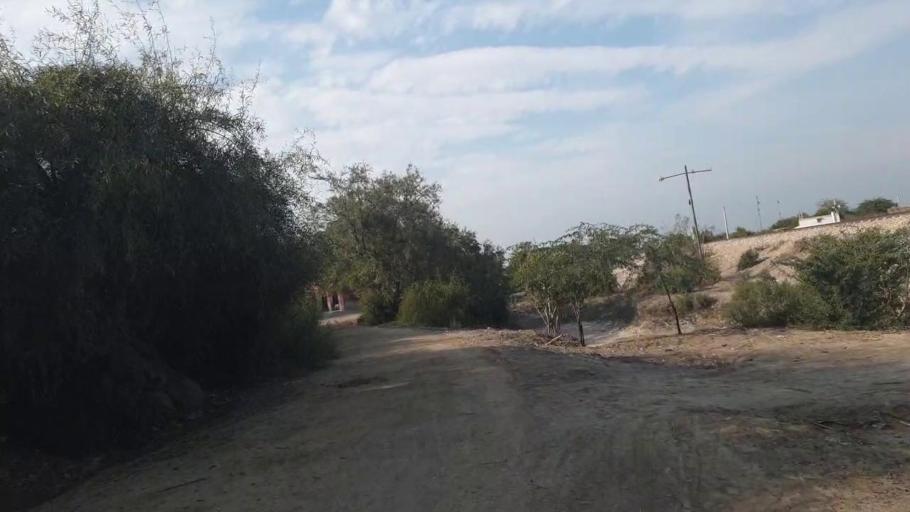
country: PK
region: Sindh
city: Shahdadpur
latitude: 26.0410
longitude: 68.5335
